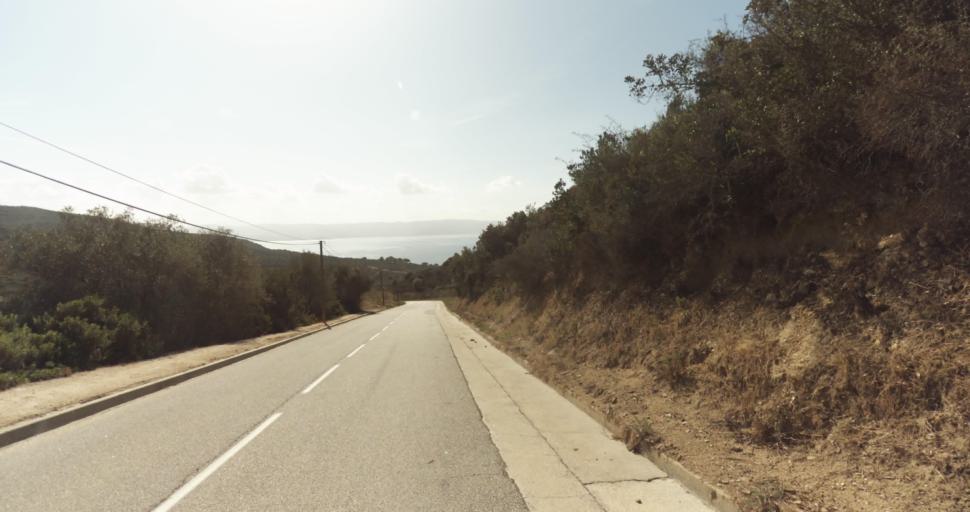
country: FR
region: Corsica
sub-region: Departement de la Corse-du-Sud
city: Ajaccio
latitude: 41.9168
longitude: 8.6422
